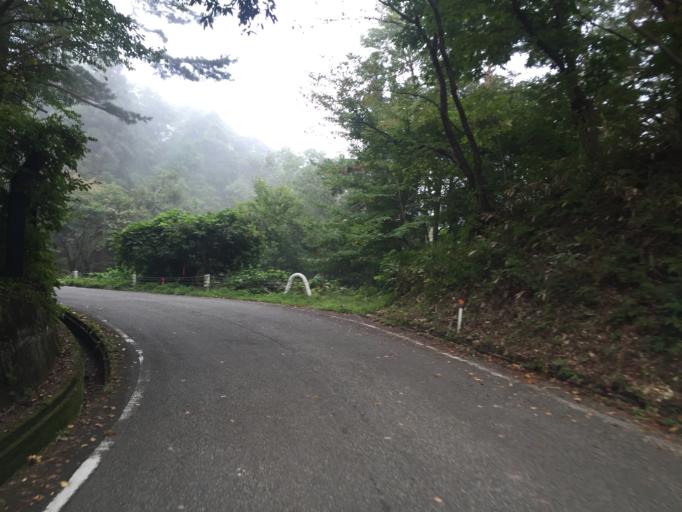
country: JP
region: Fukushima
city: Inawashiro
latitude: 37.4853
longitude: 139.9696
